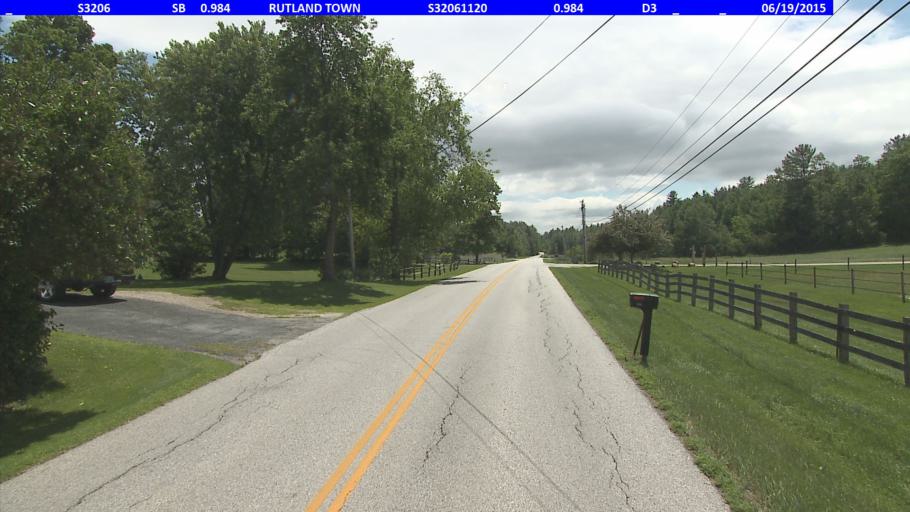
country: US
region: Vermont
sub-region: Rutland County
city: Rutland
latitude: 43.6433
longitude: -72.9935
